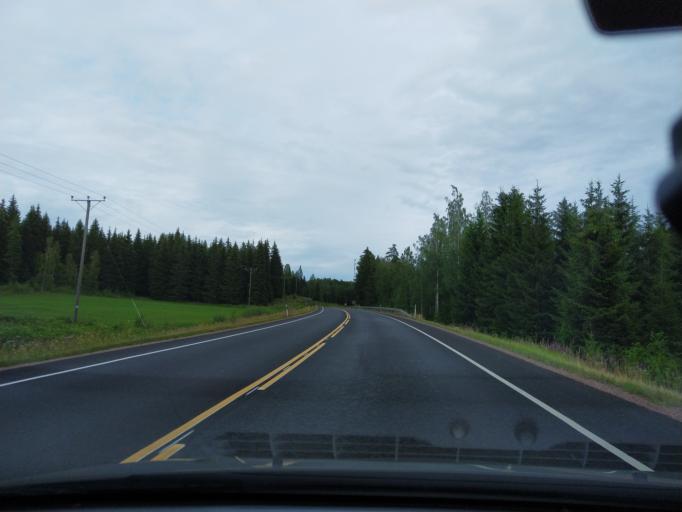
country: FI
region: Kymenlaakso
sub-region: Kouvola
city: Jaala
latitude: 61.0443
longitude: 26.5394
